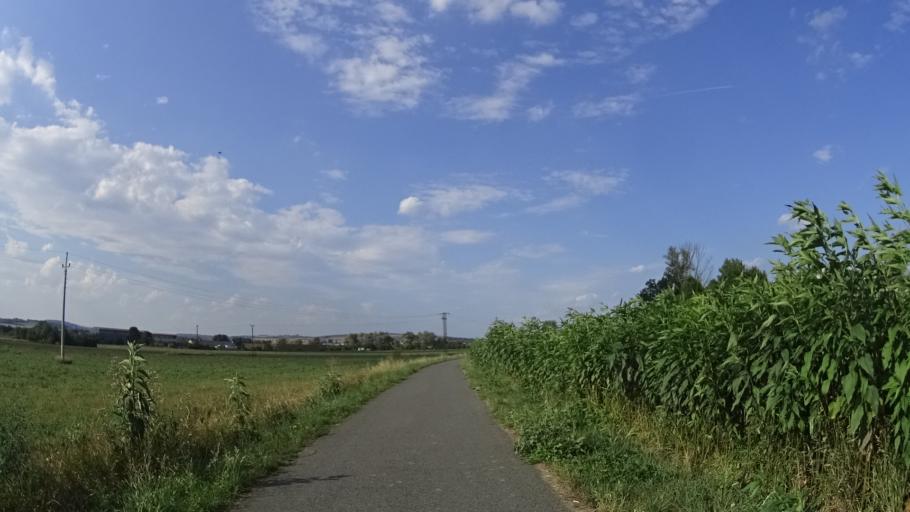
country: CZ
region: Zlin
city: Babice
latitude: 49.1217
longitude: 17.4888
